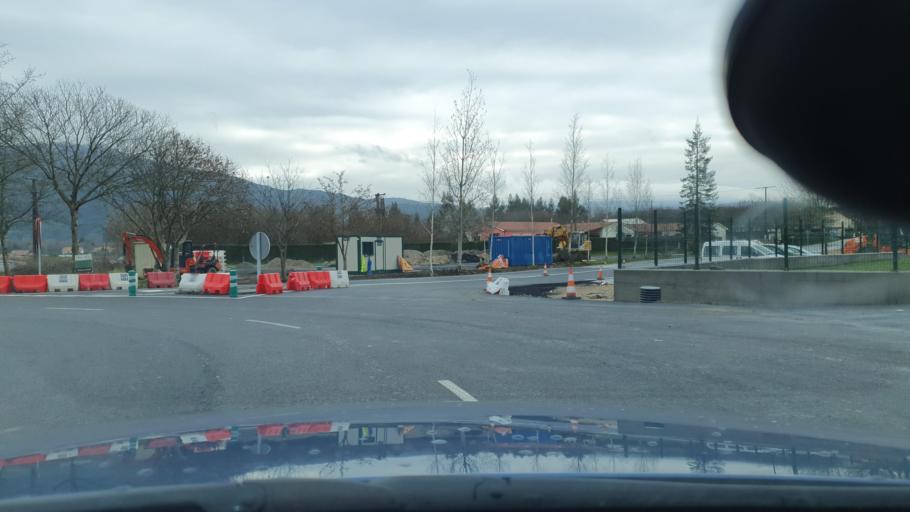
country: ES
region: Galicia
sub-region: Provincia da Coruna
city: Padron
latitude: 42.7569
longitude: -8.6704
